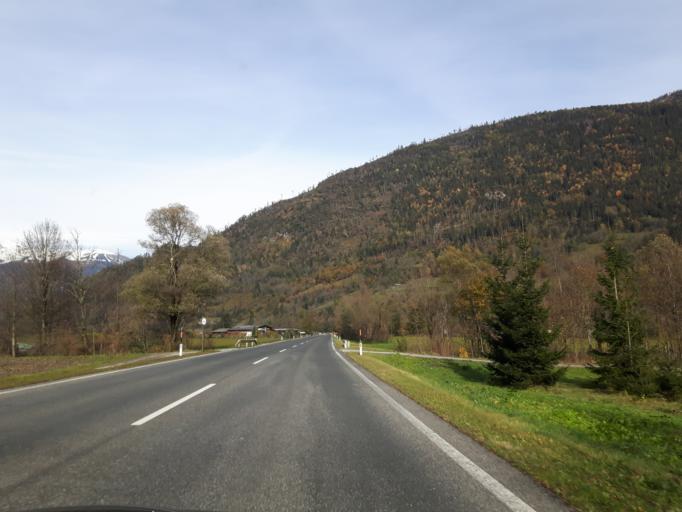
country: AT
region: Tyrol
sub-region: Politischer Bezirk Lienz
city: Lavant
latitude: 46.7929
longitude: 12.8754
